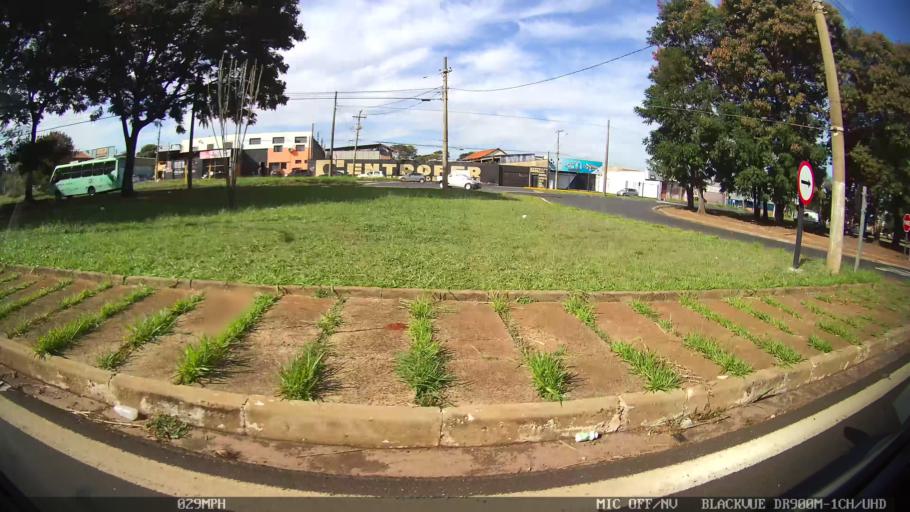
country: BR
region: Sao Paulo
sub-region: Araraquara
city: Araraquara
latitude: -21.8176
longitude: -48.1572
